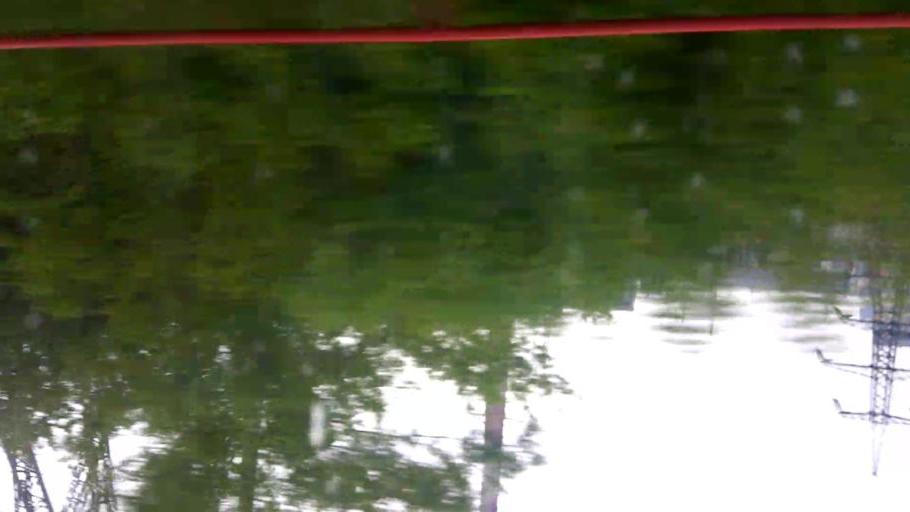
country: RU
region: Moskovskaya
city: Ozherel'ye
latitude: 54.8526
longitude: 38.2552
